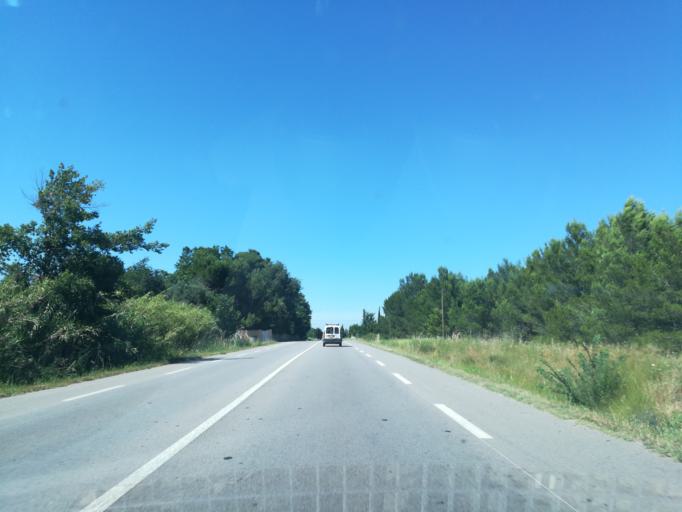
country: FR
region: Languedoc-Roussillon
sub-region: Departement des Pyrenees-Orientales
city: Pollestres
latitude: 42.6118
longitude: 2.8623
